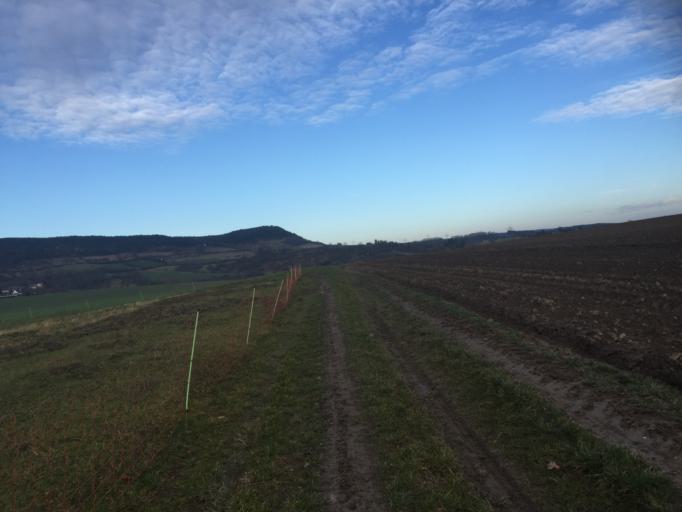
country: DE
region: Thuringia
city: Orlamunde
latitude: 50.7624
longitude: 11.5001
